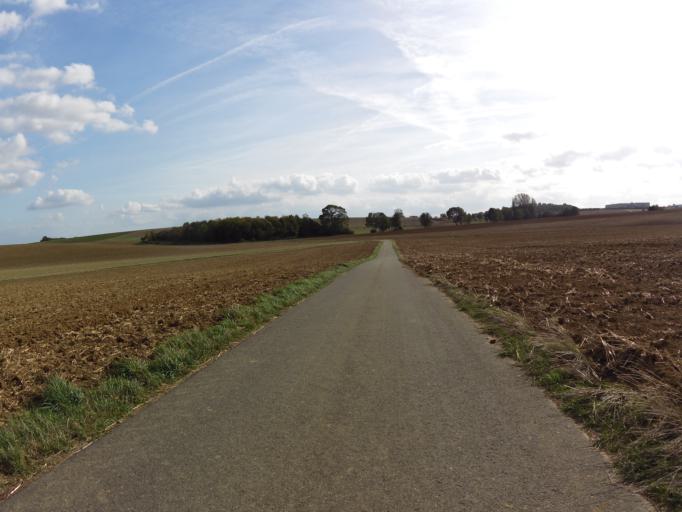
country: DE
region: Bavaria
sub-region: Regierungsbezirk Unterfranken
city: Reichenberg
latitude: 49.7063
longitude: 9.9485
